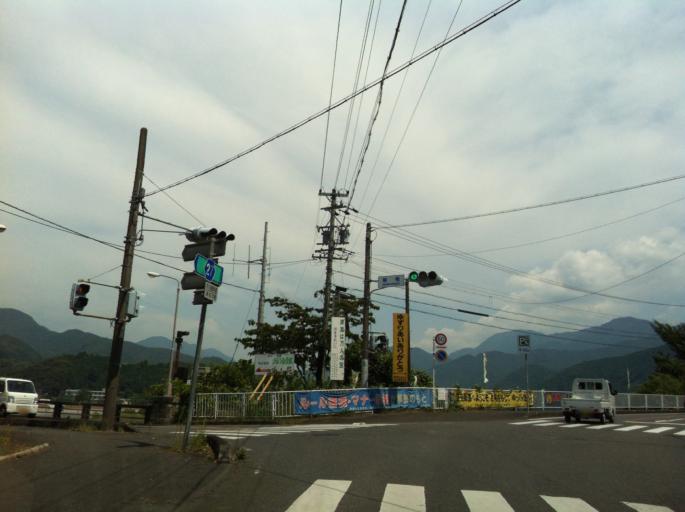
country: JP
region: Shizuoka
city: Shizuoka-shi
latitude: 35.0708
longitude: 138.3700
